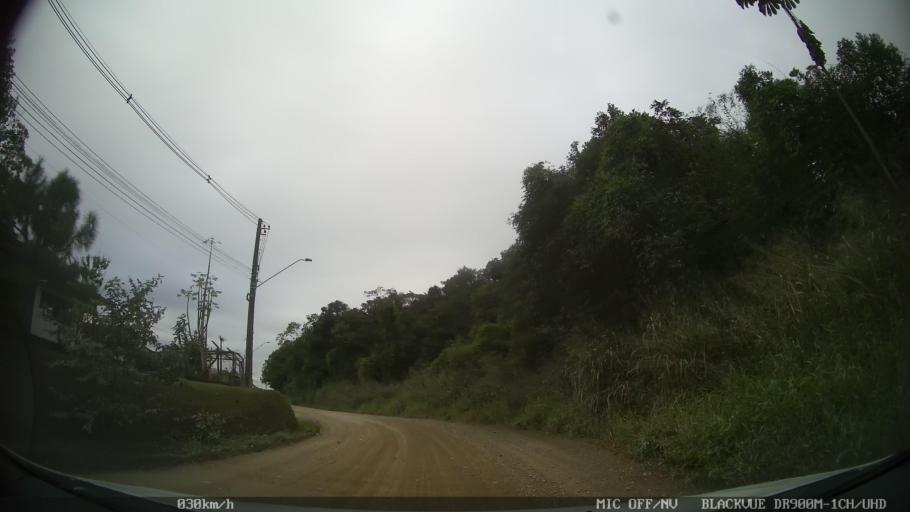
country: BR
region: Santa Catarina
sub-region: Joinville
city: Joinville
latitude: -26.2503
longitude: -48.9253
